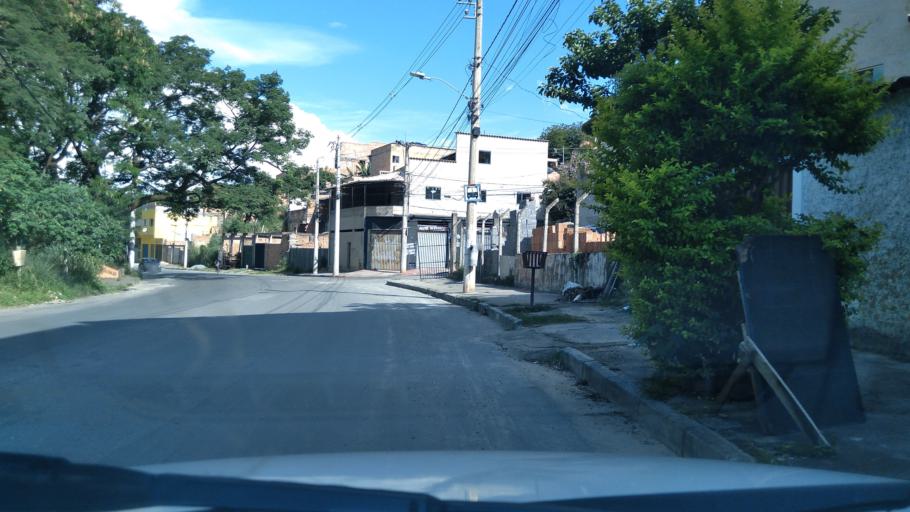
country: BR
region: Minas Gerais
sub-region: Santa Luzia
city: Santa Luzia
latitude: -19.8562
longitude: -43.8721
